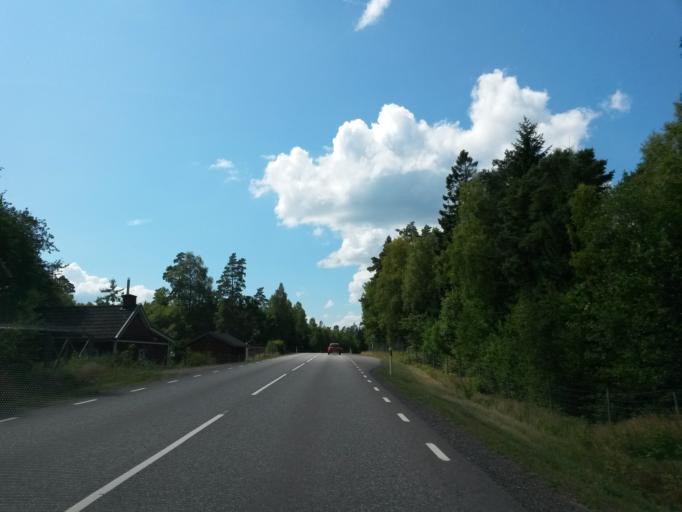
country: SE
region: Vaestra Goetaland
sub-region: Lerums Kommun
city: Grabo
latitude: 57.9323
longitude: 12.3745
